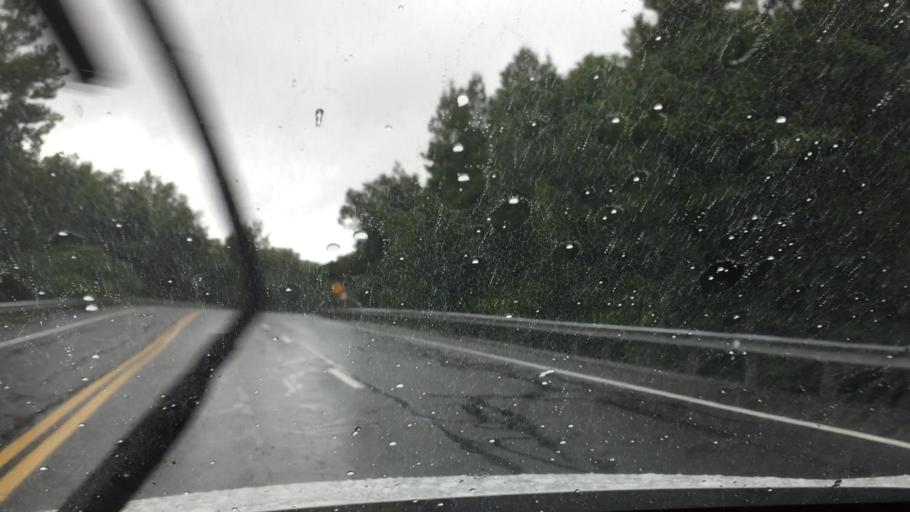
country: US
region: Massachusetts
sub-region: Berkshire County
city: Lanesborough
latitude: 42.4954
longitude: -73.2207
